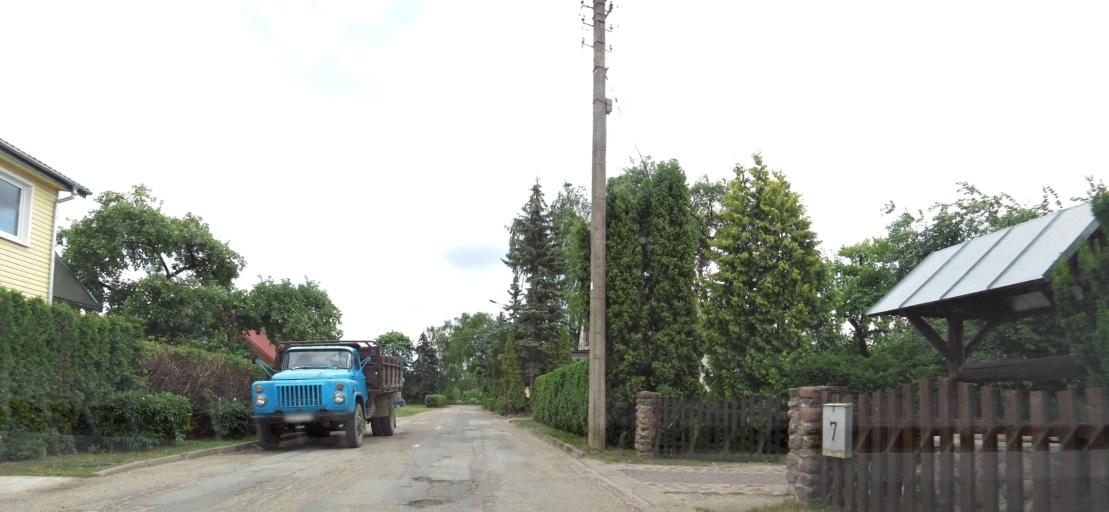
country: LT
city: Kupiskis
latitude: 55.8377
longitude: 24.9683
